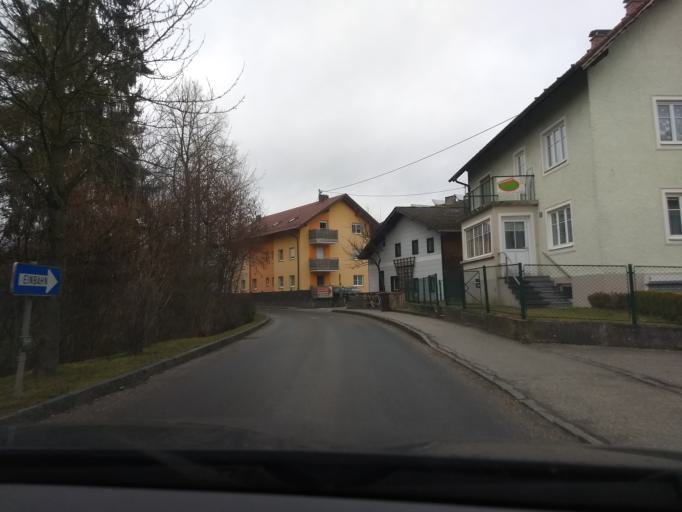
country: AT
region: Upper Austria
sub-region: Politischer Bezirk Grieskirchen
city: Grieskirchen
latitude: 48.3446
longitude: 13.7738
